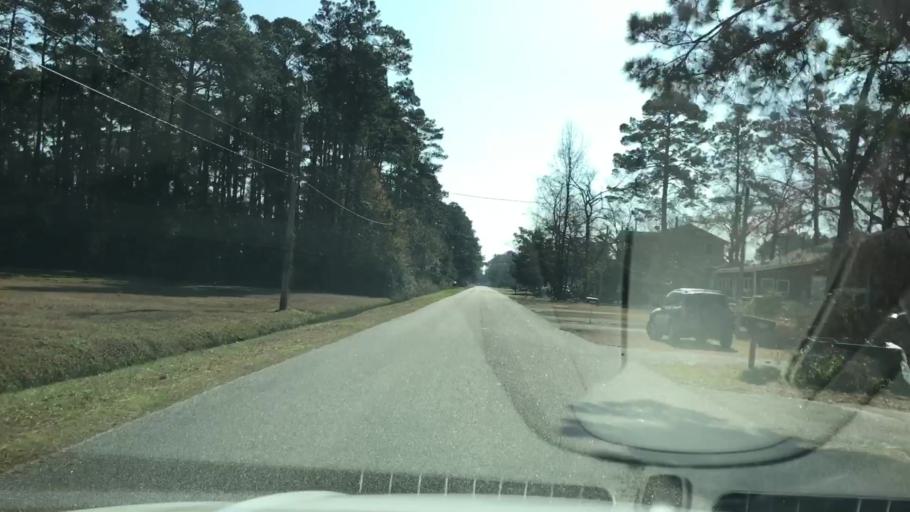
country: US
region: South Carolina
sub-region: Horry County
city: Garden City
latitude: 33.5880
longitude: -79.0066
